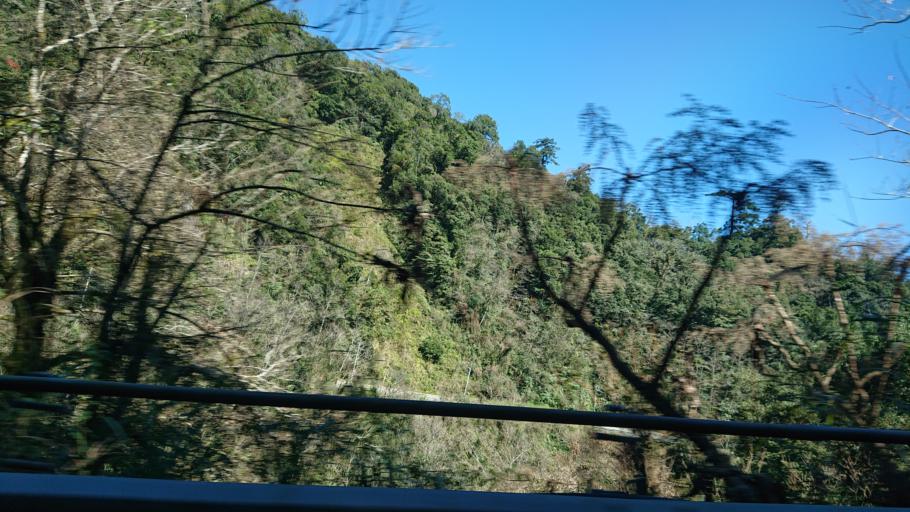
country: TW
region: Taiwan
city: Daxi
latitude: 24.4116
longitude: 121.3600
